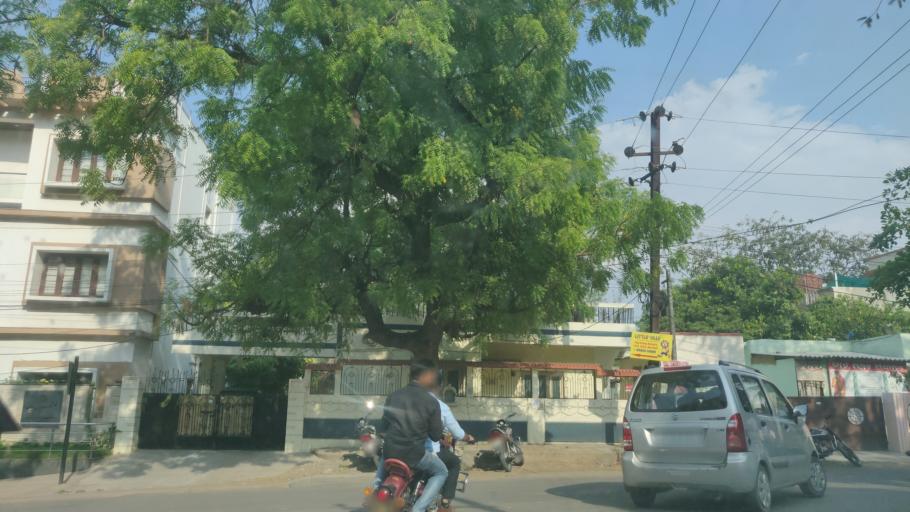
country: IN
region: Telangana
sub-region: Rangareddi
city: Gaddi Annaram
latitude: 17.3756
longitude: 78.5193
